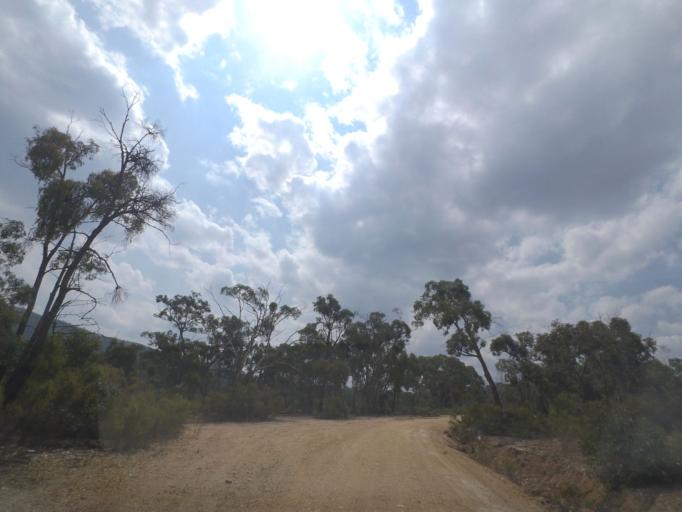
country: AU
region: Victoria
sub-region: Moorabool
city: Bacchus Marsh
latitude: -37.5729
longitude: 144.4380
